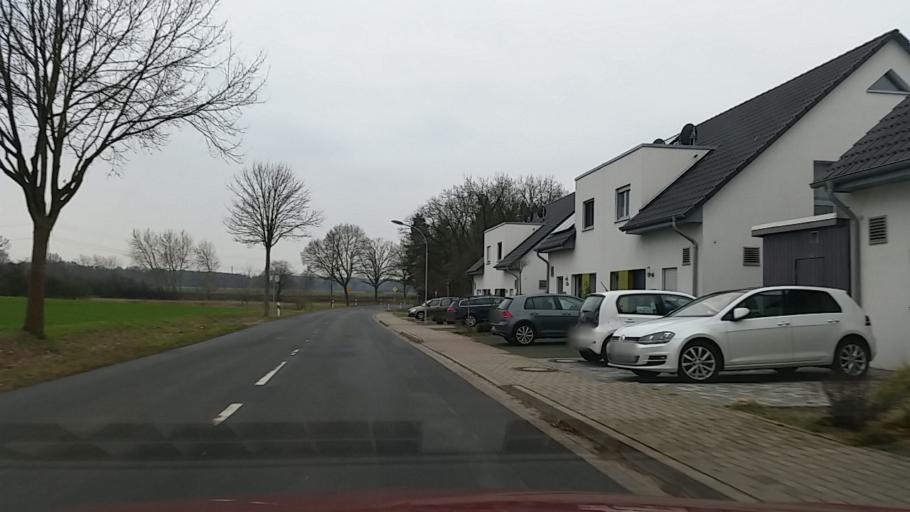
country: DE
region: Lower Saxony
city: Wasbuttel
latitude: 52.3779
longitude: 10.5854
